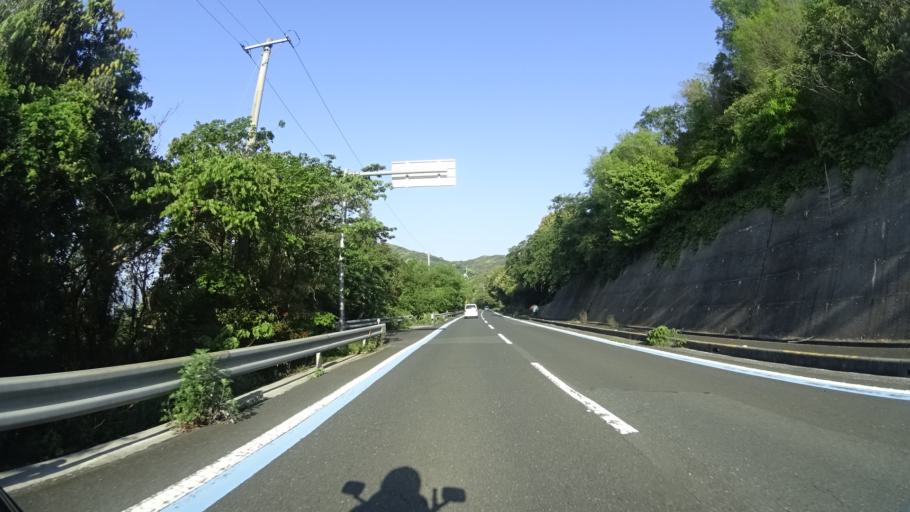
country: JP
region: Ehime
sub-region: Nishiuwa-gun
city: Ikata-cho
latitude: 33.4196
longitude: 132.1891
